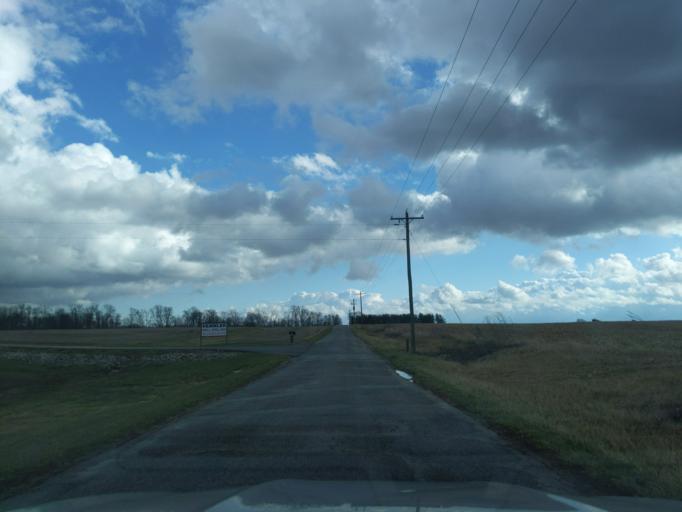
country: US
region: Indiana
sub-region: Decatur County
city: Saint Paul
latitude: 39.4093
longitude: -85.5552
